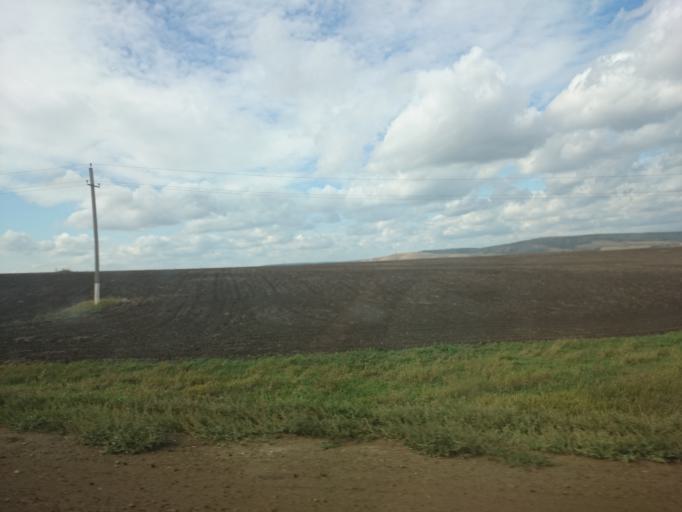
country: RU
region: Samara
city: Kamyshla
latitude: 54.0701
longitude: 52.1811
